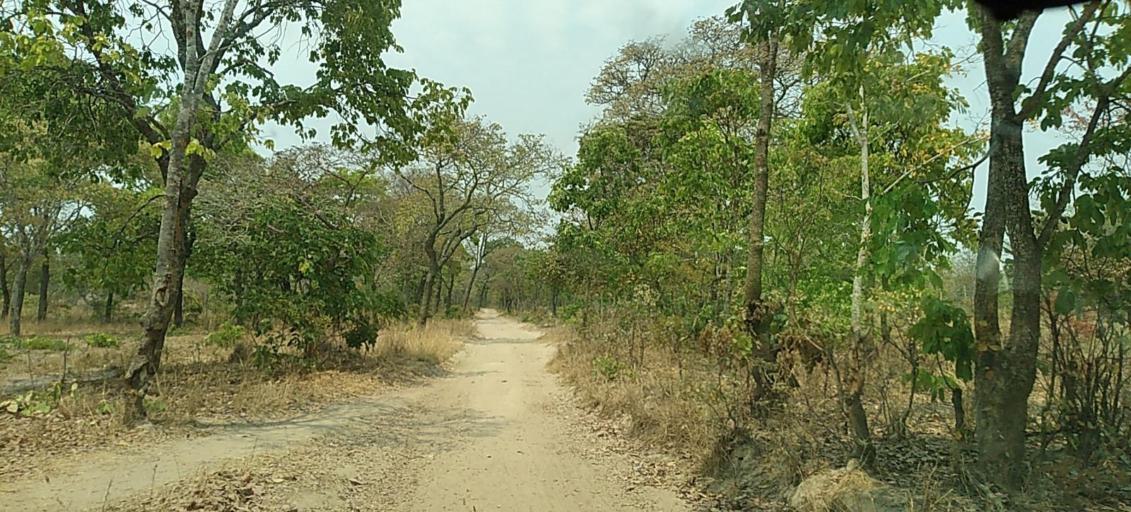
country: ZM
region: North-Western
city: Kabompo
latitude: -13.5429
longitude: 24.4512
